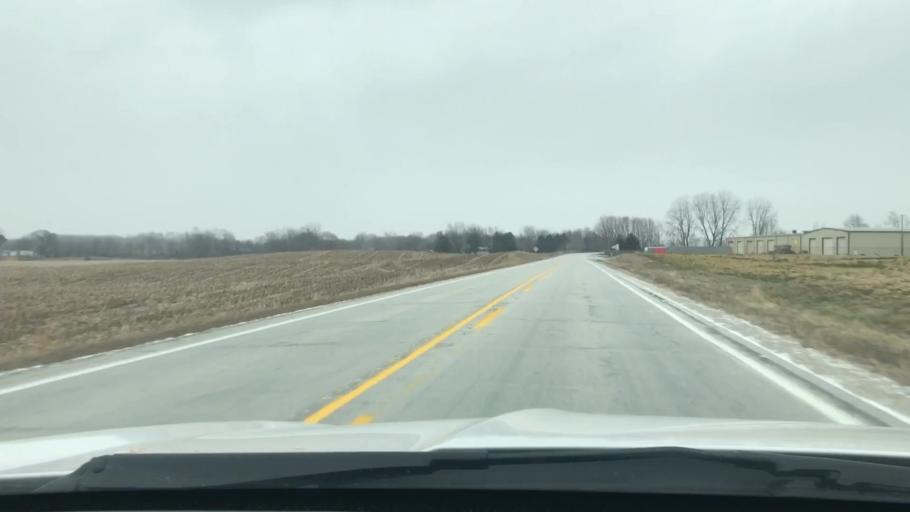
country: US
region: Indiana
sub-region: Fulton County
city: Akron
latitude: 41.0398
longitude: -86.0828
